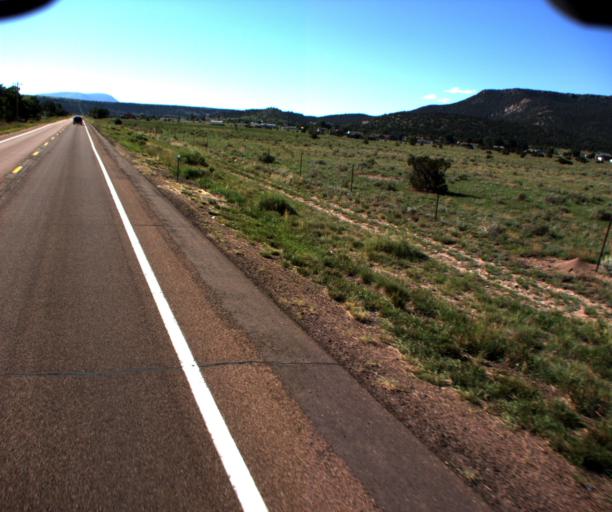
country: US
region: Arizona
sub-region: Apache County
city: Springerville
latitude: 34.1208
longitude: -109.2597
